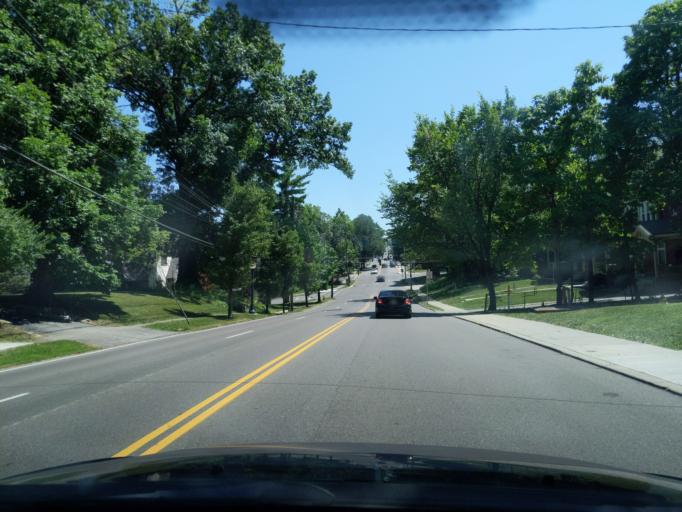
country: US
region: Ohio
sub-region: Hamilton County
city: Saint Bernard
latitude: 39.1467
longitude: -84.5189
